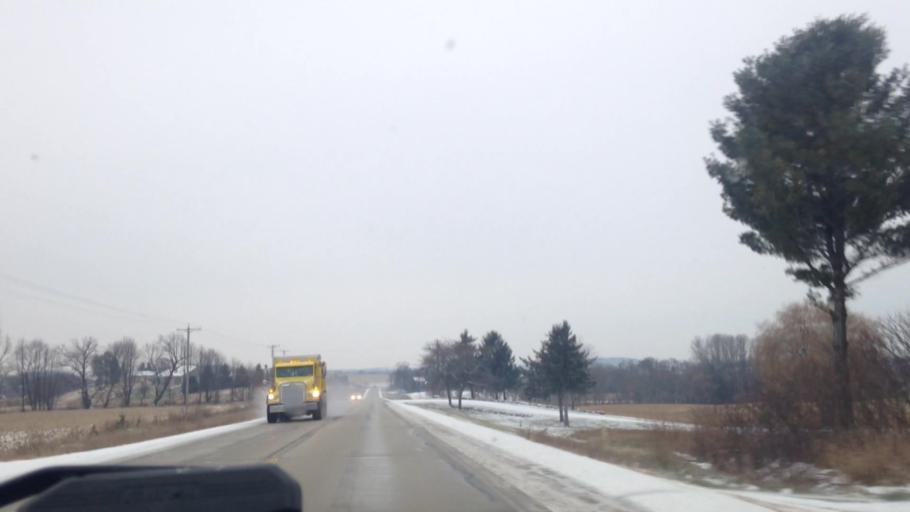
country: US
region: Wisconsin
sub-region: Dodge County
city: Hustisford
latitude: 43.2502
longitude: -88.5179
